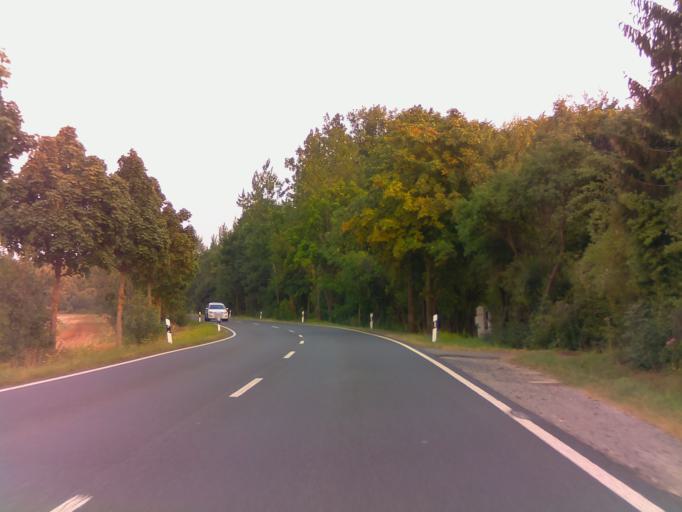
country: DE
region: Thuringia
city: Troistedt
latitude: 50.9297
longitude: 11.2481
